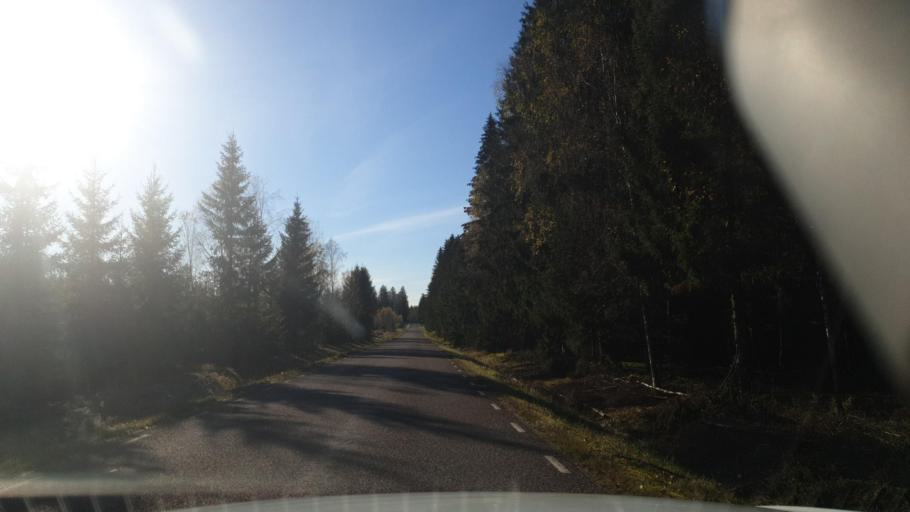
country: SE
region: Vaermland
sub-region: Karlstads Kommun
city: Edsvalla
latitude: 59.4670
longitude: 13.0837
